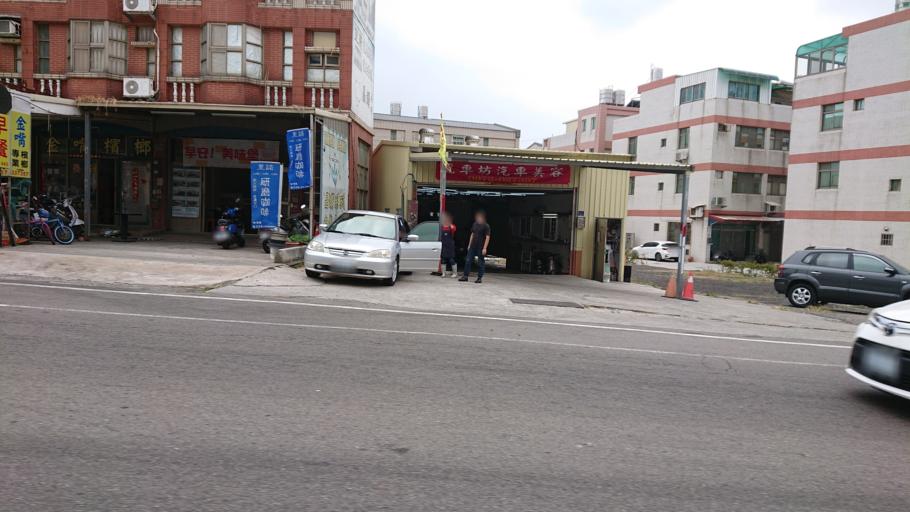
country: TW
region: Fukien
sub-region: Kinmen
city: Jincheng
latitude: 24.4371
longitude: 118.4081
